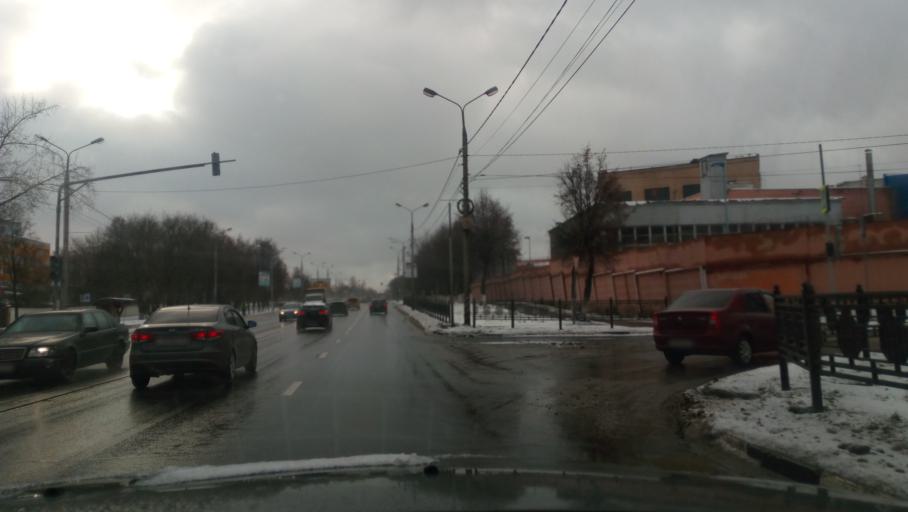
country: RU
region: Moskovskaya
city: Domodedovo
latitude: 55.4480
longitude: 37.7639
